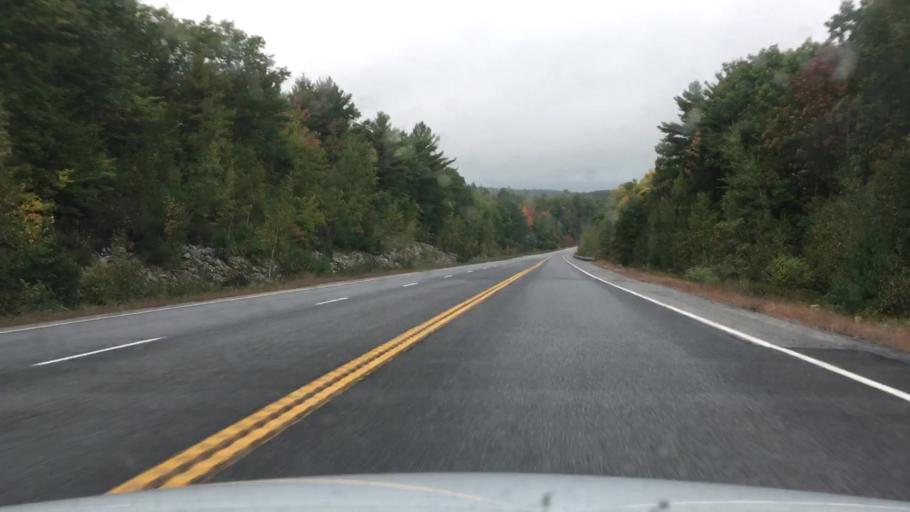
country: US
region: Maine
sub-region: Cumberland County
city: New Gloucester
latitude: 43.9622
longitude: -70.3583
